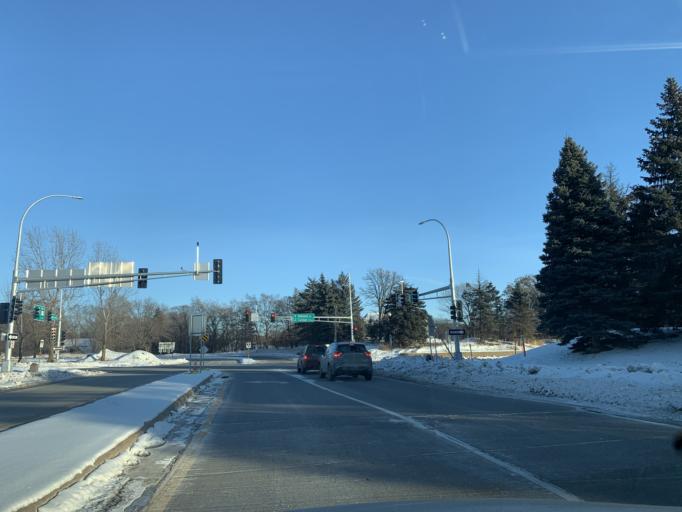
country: US
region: Minnesota
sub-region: Hennepin County
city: Wayzata
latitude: 44.9697
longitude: -93.4706
